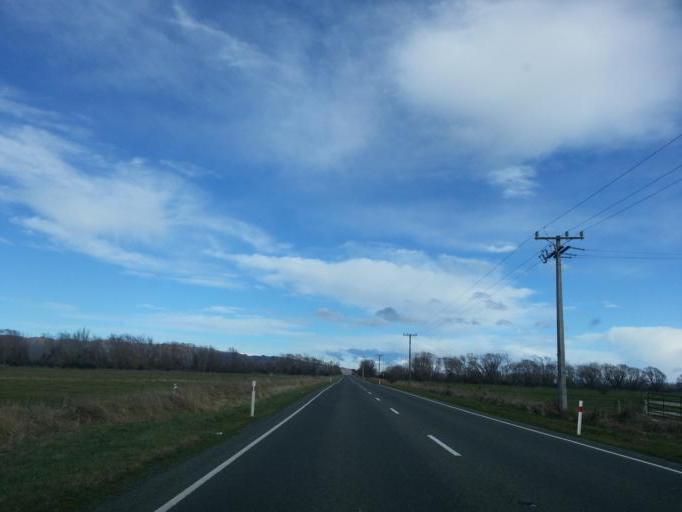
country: NZ
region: Canterbury
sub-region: Hurunui District
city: Amberley
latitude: -42.7934
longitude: 172.8326
